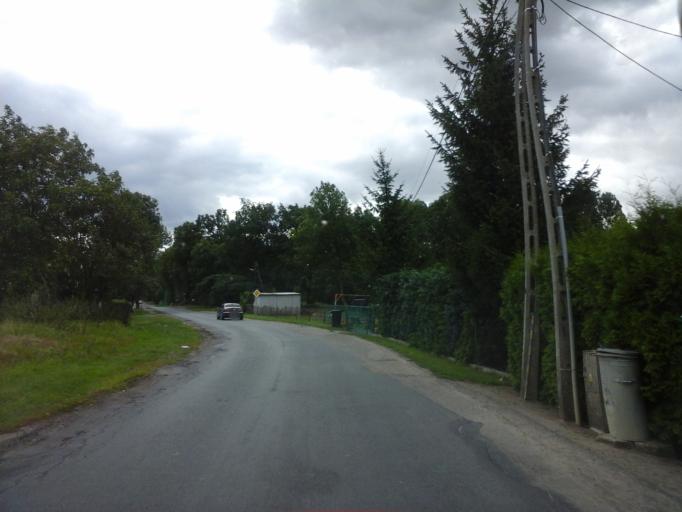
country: PL
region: West Pomeranian Voivodeship
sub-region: Powiat policki
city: Przeclaw
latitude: 53.3952
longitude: 14.4393
